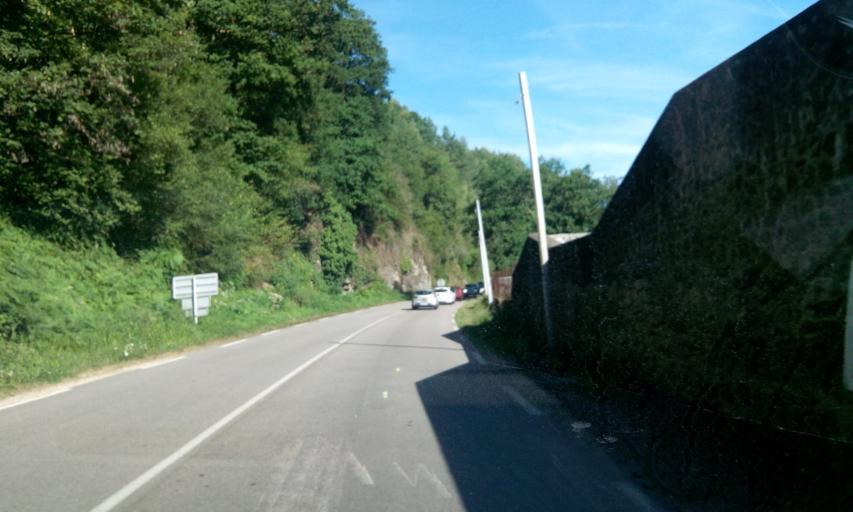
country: FR
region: Limousin
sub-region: Departement de la Haute-Vienne
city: Saint-Leonard-de-Noblat
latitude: 45.8369
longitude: 1.4692
